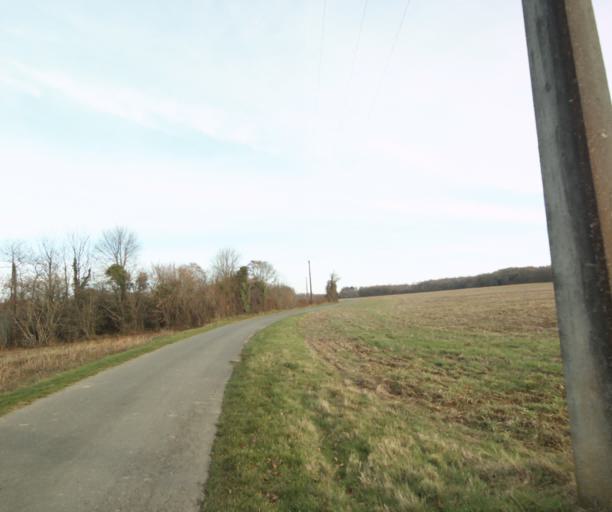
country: FR
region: Poitou-Charentes
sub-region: Departement de la Charente-Maritime
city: Saint-Hilaire-de-Villefranche
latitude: 45.8353
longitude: -0.5723
